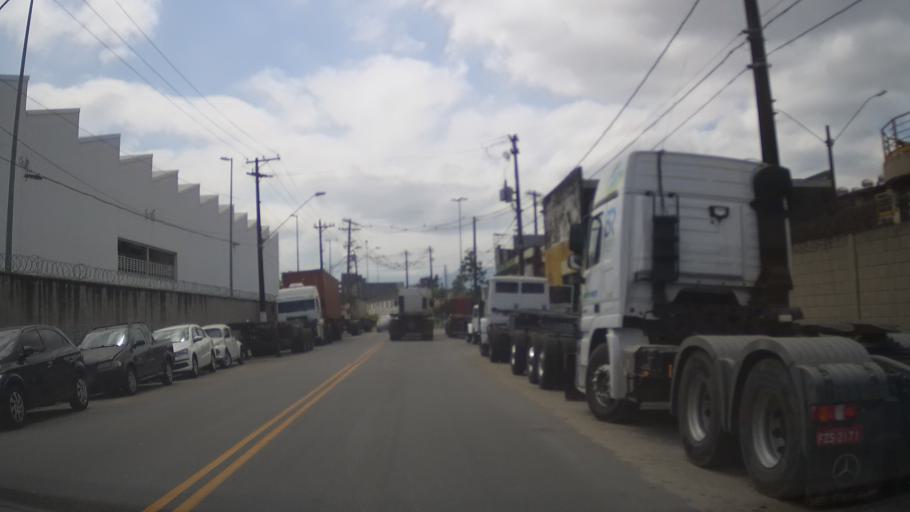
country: BR
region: Sao Paulo
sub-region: Santos
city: Santos
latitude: -23.9533
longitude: -46.3130
